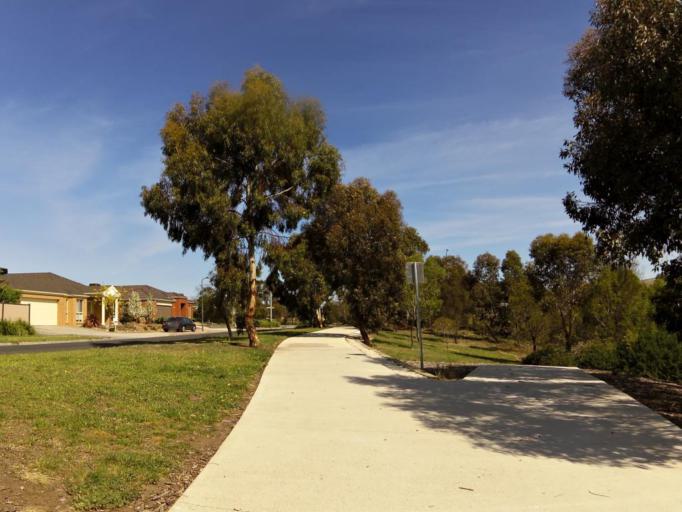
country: AU
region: Victoria
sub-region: Brimbank
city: Deer Park
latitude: -37.7644
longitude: 144.7825
